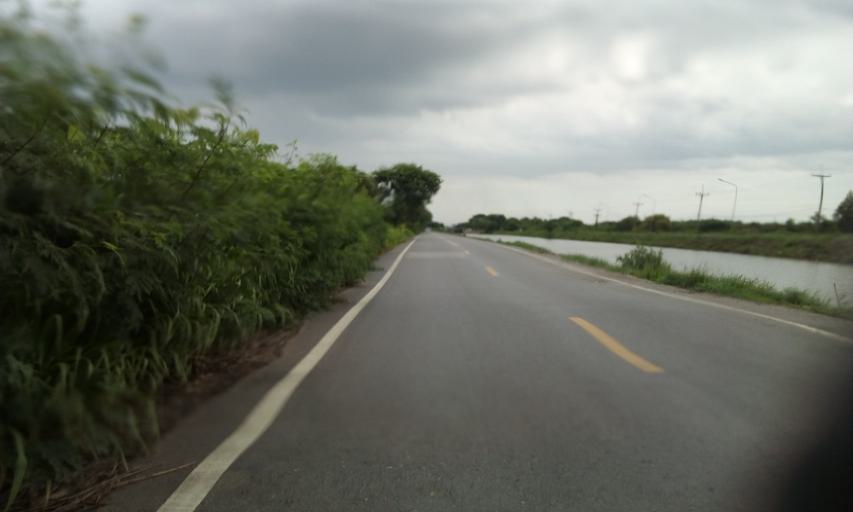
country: TH
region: Pathum Thani
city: Nong Suea
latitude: 14.0660
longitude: 100.8468
